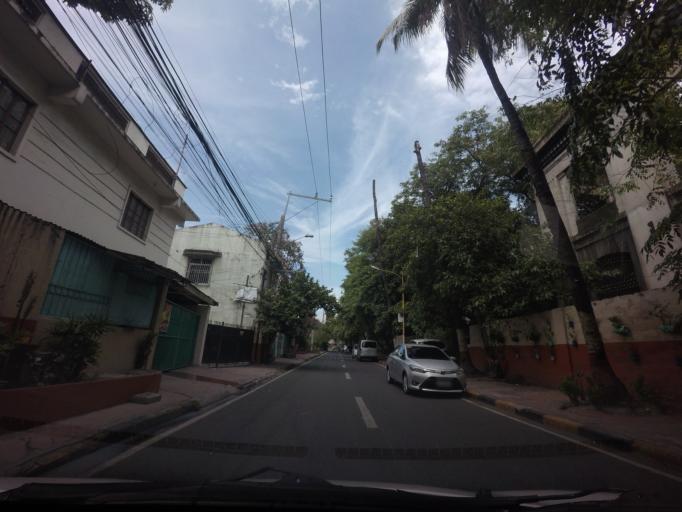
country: PH
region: Calabarzon
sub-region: Province of Rizal
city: Pateros
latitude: 14.5570
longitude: 121.0722
